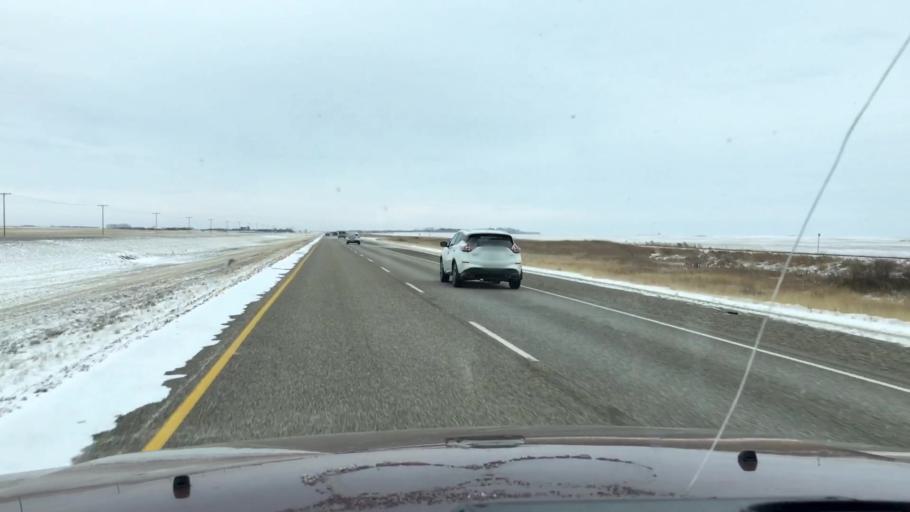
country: CA
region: Saskatchewan
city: Moose Jaw
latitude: 50.9930
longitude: -105.7557
